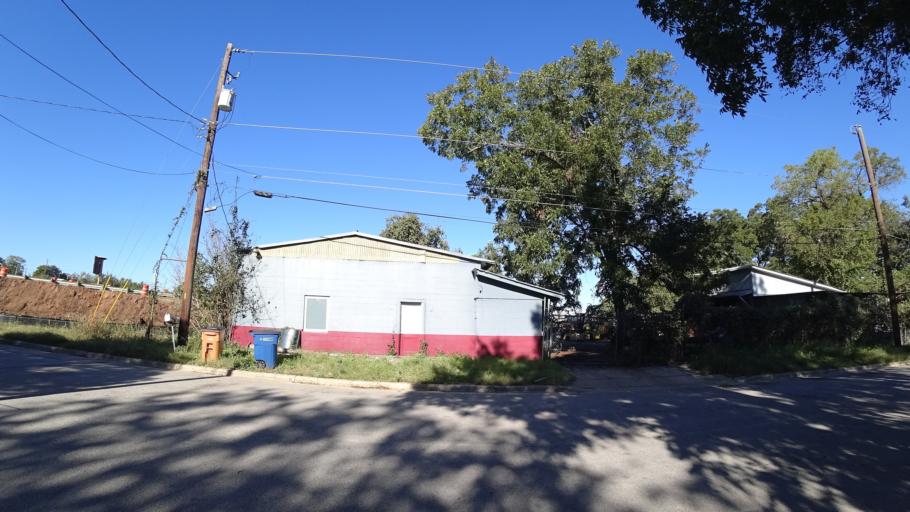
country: US
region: Texas
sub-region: Travis County
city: Austin
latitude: 30.2444
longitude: -97.6896
